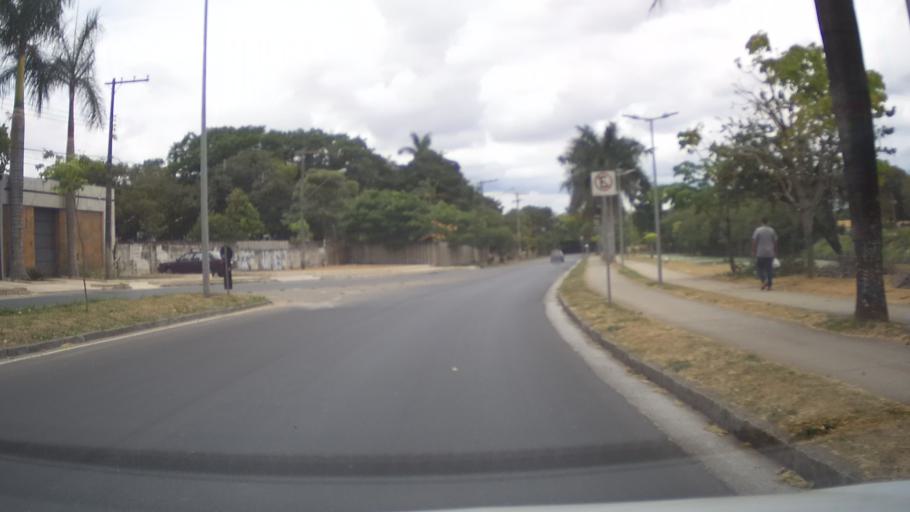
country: BR
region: Minas Gerais
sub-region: Belo Horizonte
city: Belo Horizonte
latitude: -19.8570
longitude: -43.9984
